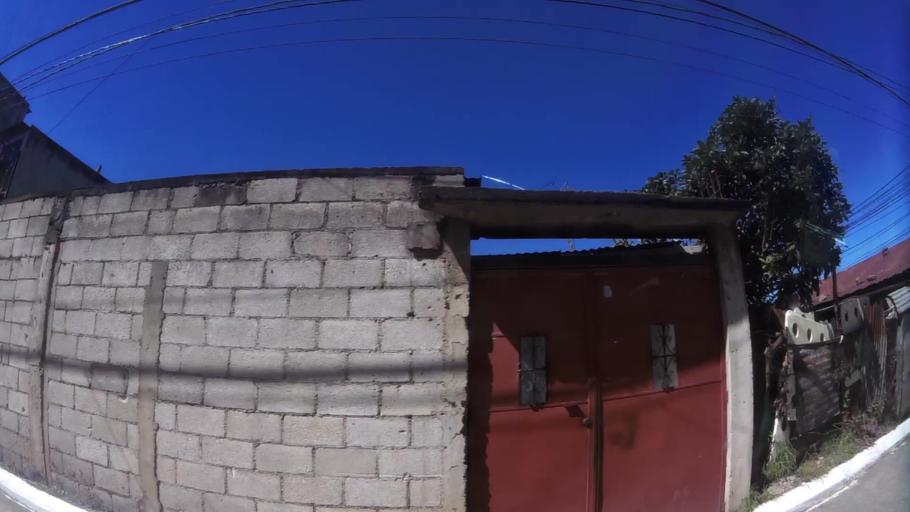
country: GT
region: Guatemala
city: San Jose Pinula
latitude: 14.5423
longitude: -90.4119
